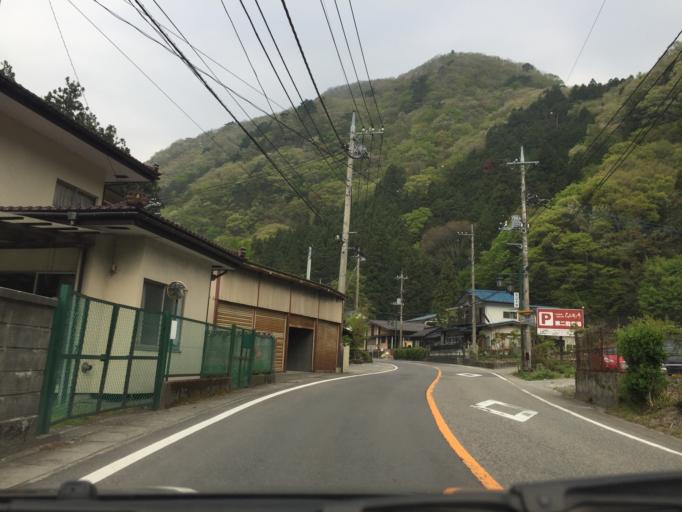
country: JP
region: Tochigi
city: Nikko
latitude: 36.8960
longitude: 139.7080
